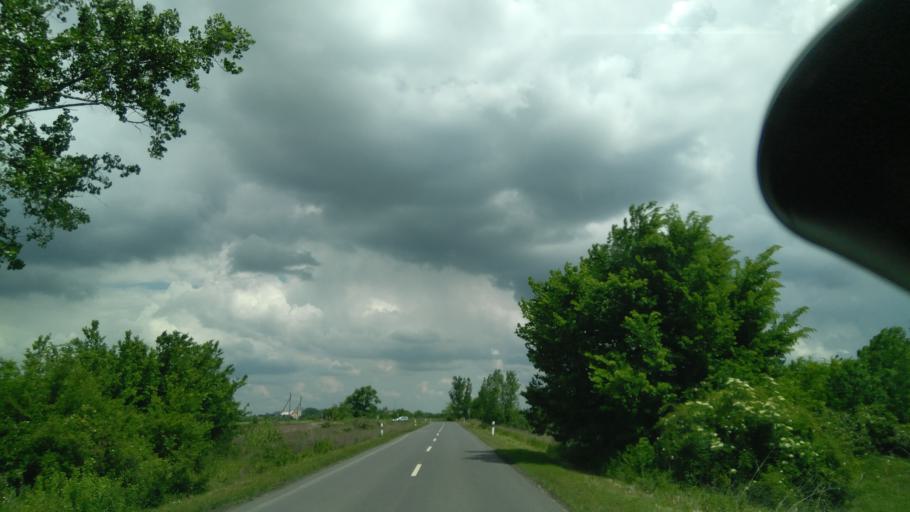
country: HU
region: Bekes
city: Devavanya
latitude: 47.0165
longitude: 20.9318
